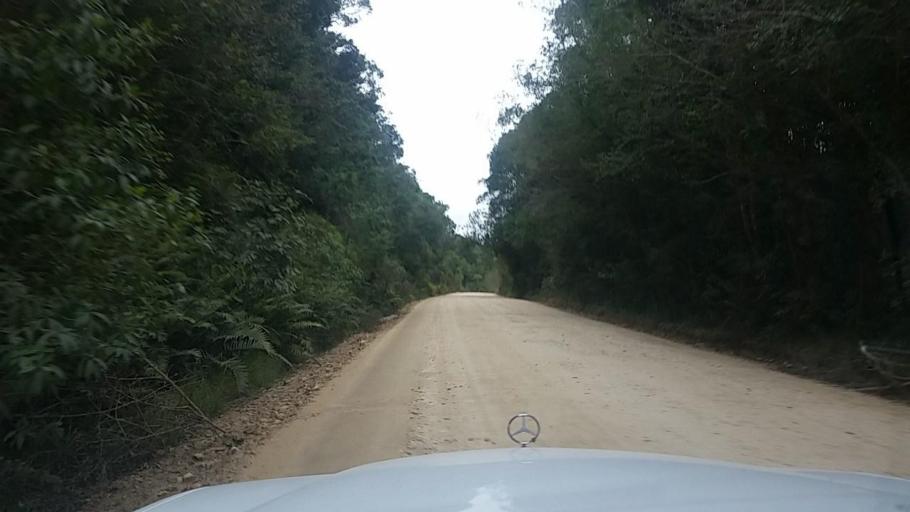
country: ZA
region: Western Cape
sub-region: Eden District Municipality
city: Knysna
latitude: -33.9593
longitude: 23.1577
